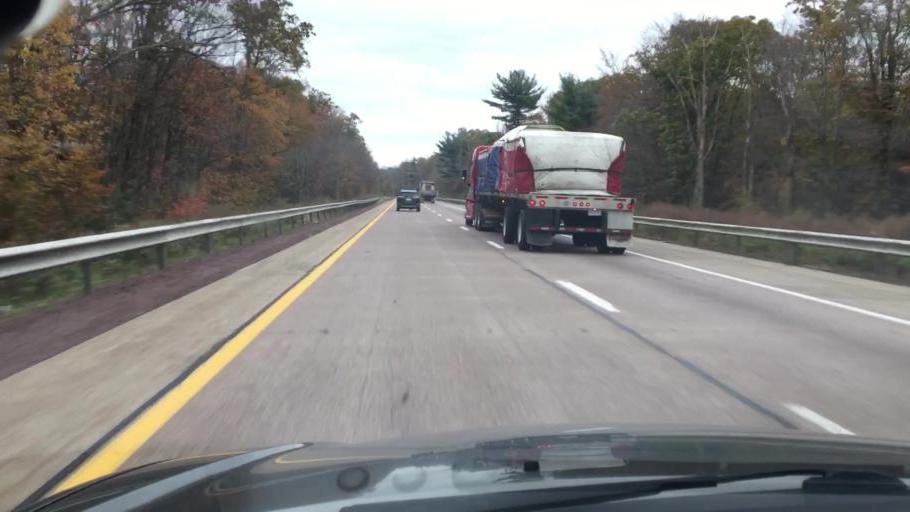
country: US
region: Pennsylvania
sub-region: Luzerne County
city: Freeland
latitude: 41.0589
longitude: -75.8623
